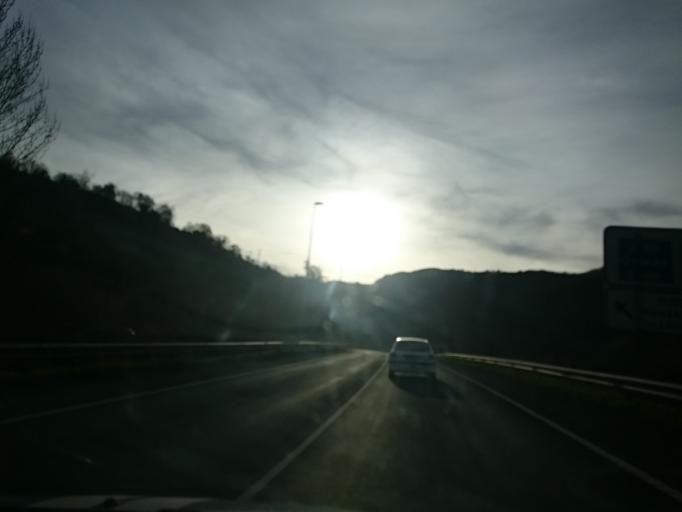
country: ES
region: Asturias
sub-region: Province of Asturias
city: Oviedo
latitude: 43.2993
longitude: -5.8307
